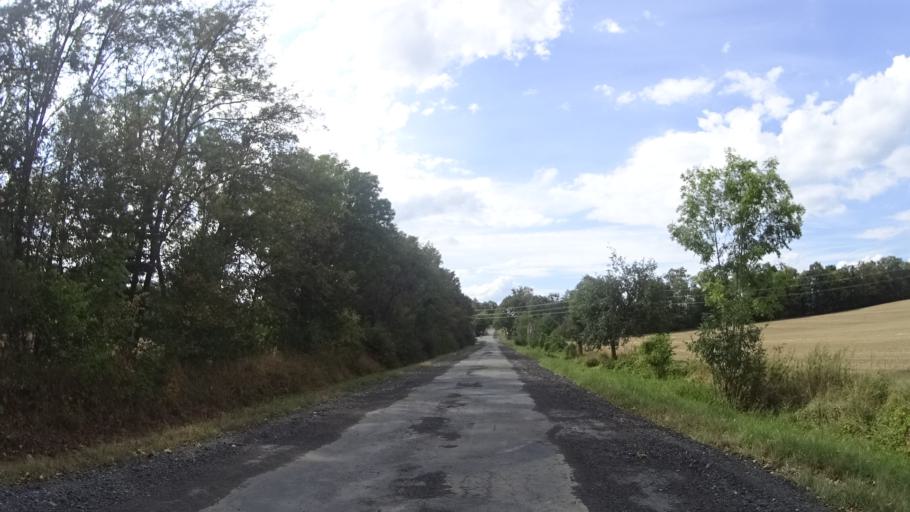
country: CZ
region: Olomoucky
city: Cervenka
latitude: 49.7198
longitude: 17.0353
